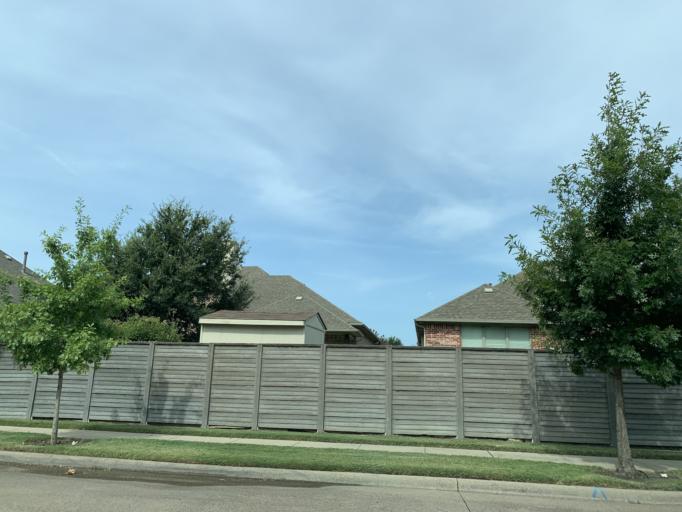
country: US
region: Texas
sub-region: Dallas County
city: Grand Prairie
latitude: 32.6589
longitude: -97.0099
